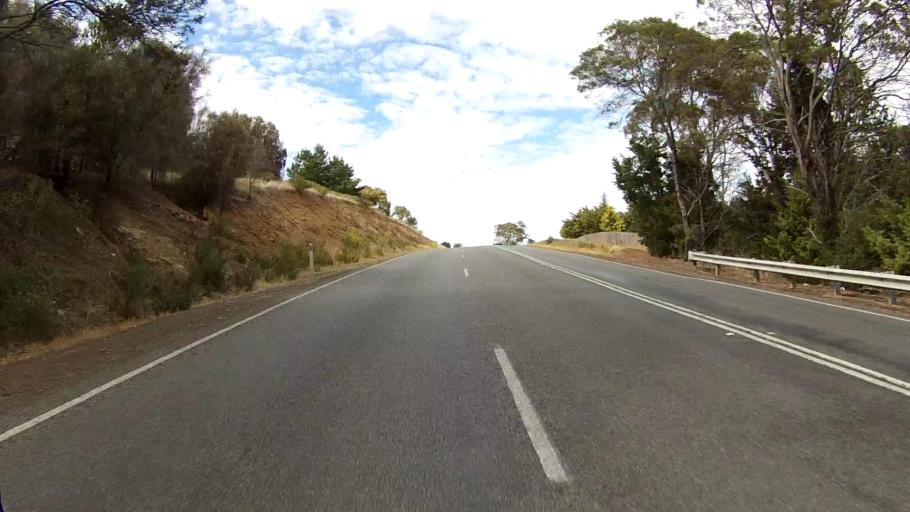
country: AU
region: Tasmania
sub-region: Brighton
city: Old Beach
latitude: -42.7910
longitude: 147.2932
